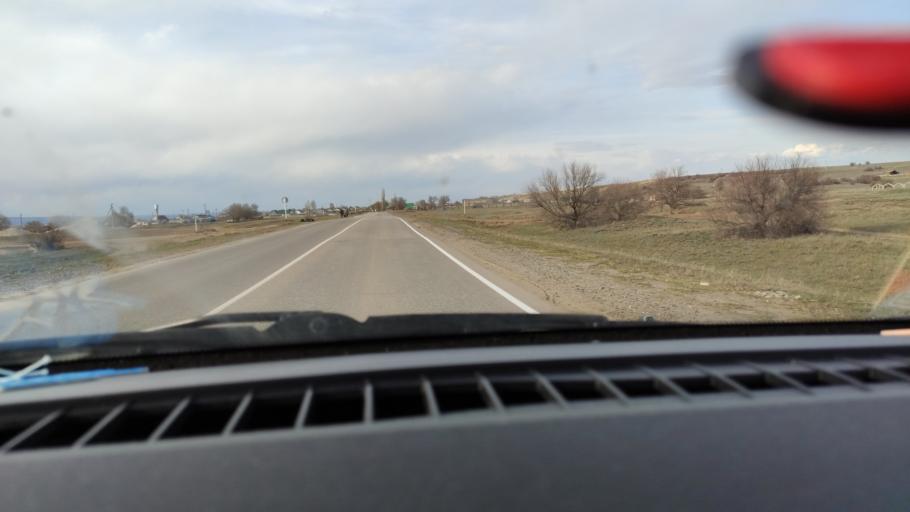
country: RU
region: Saratov
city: Privolzhskiy
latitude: 51.1984
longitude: 45.9158
